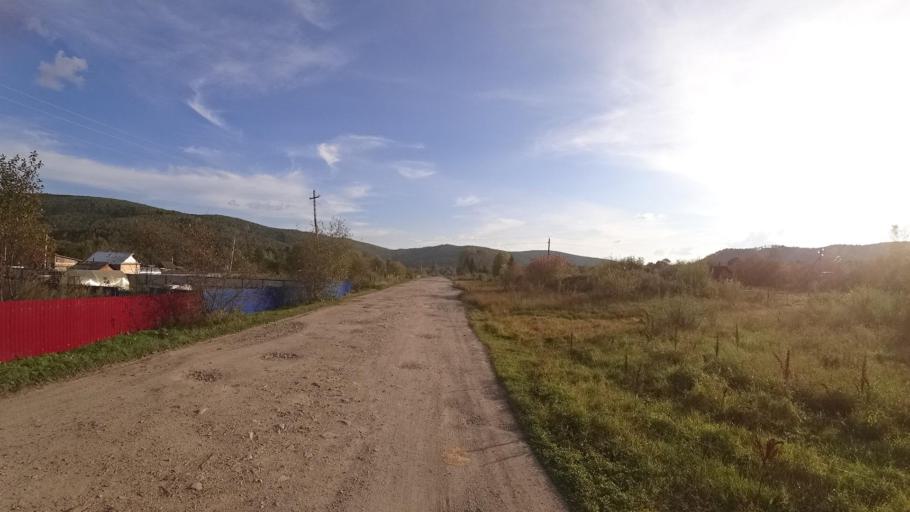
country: RU
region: Jewish Autonomous Oblast
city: Kul'dur
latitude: 49.2004
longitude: 131.6264
